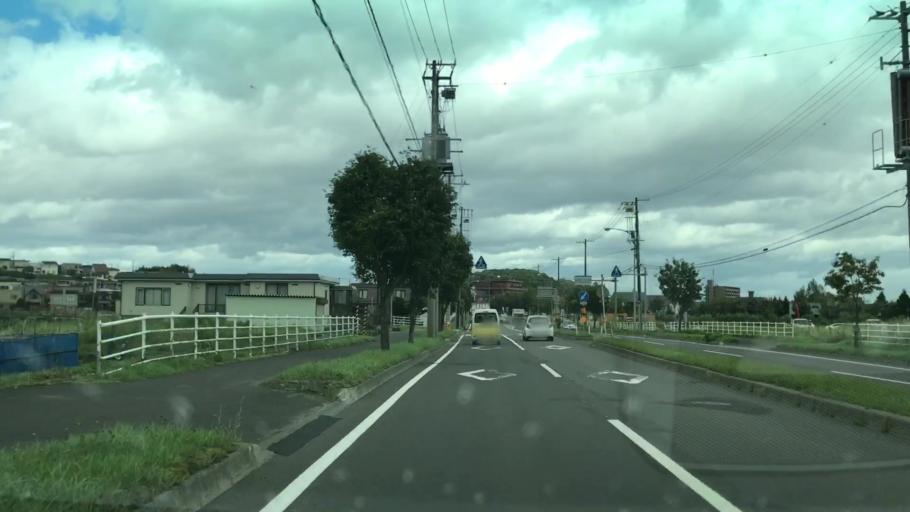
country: JP
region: Hokkaido
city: Sapporo
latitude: 42.9803
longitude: 141.4385
